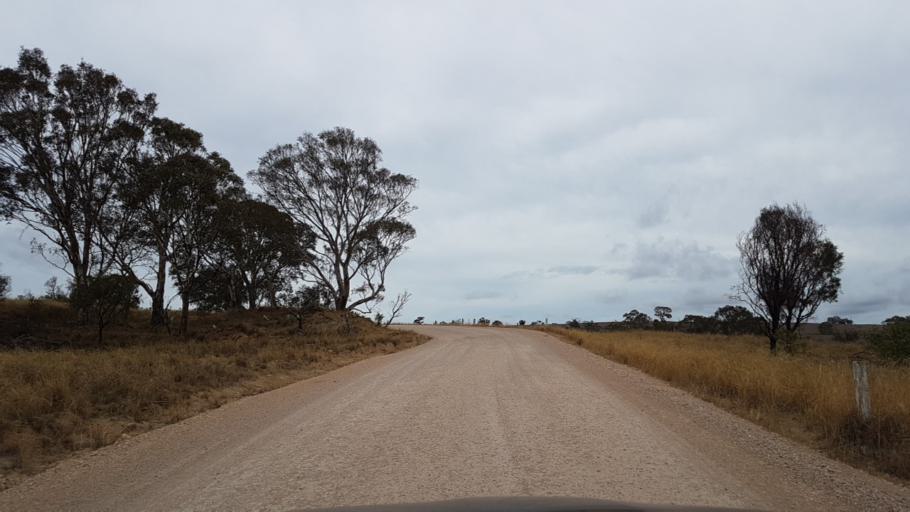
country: AU
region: South Australia
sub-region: Adelaide Hills
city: Birdwood
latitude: -34.8796
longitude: 139.0830
